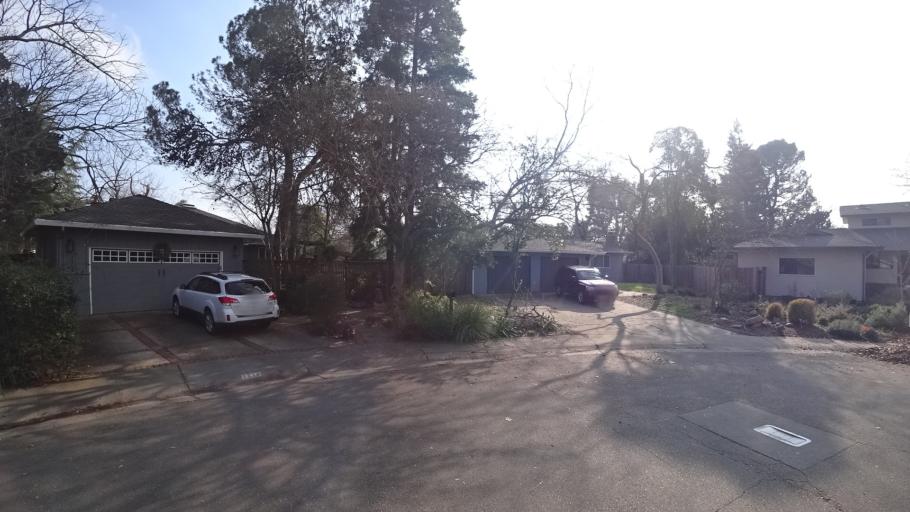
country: US
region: California
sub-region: Yolo County
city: Davis
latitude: 38.5555
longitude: -121.7452
